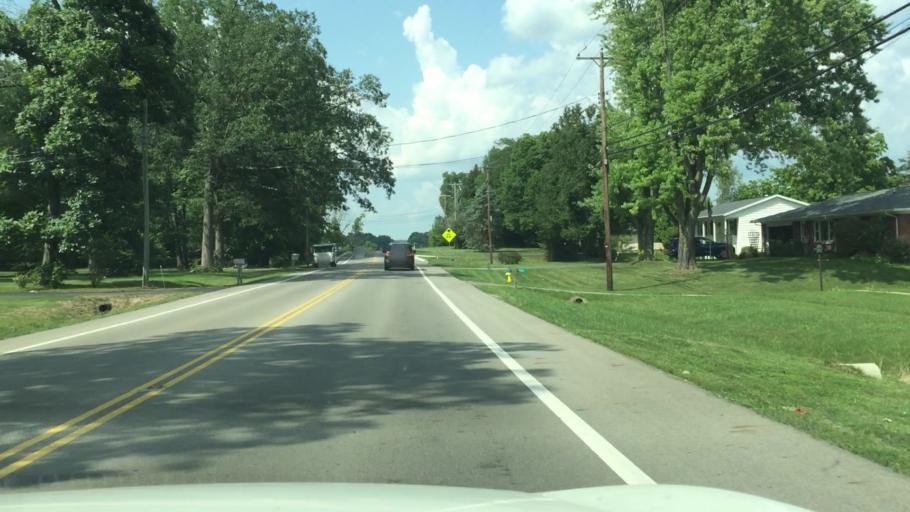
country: US
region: Ohio
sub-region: Clark County
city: Northridge
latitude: 39.9715
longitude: -83.7846
